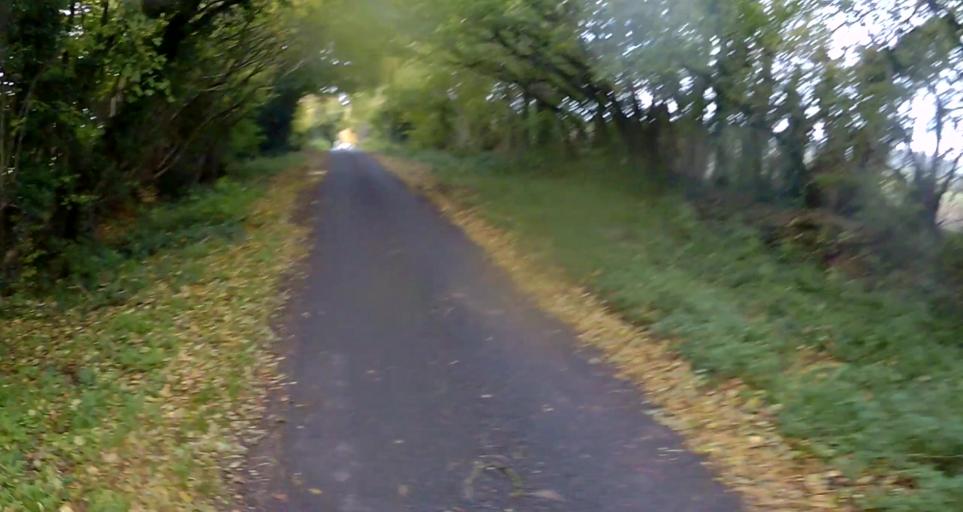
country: GB
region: England
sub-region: Hampshire
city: Four Marks
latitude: 51.1569
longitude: -1.0674
